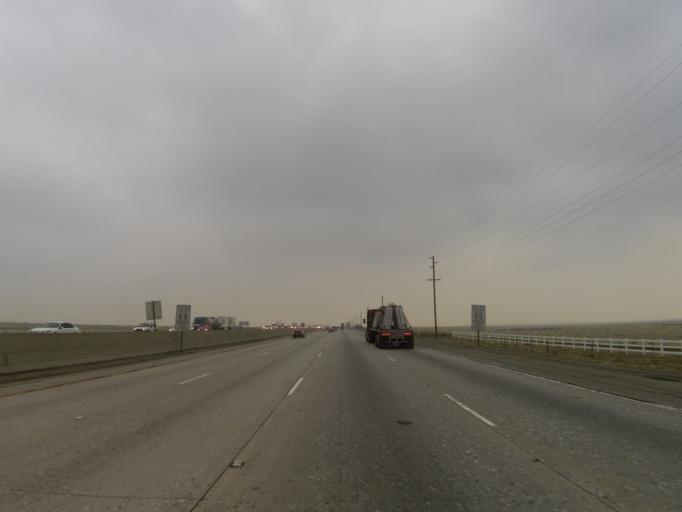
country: US
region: California
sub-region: Kern County
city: Frazier Park
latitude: 34.9451
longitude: -118.9321
